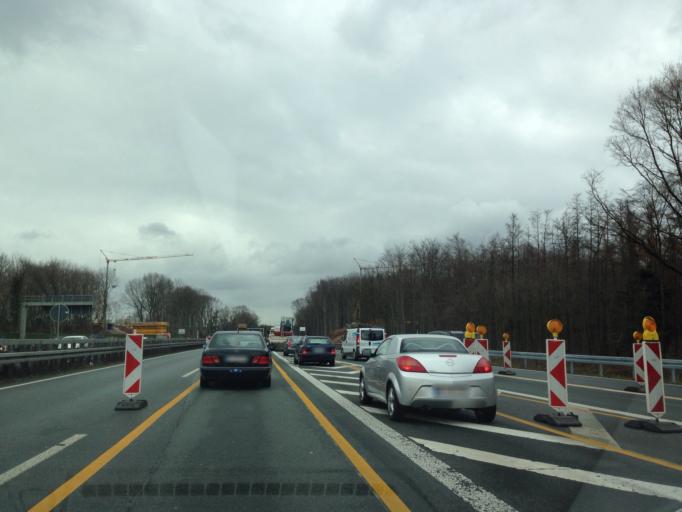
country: DE
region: North Rhine-Westphalia
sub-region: Regierungsbezirk Munster
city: Recklinghausen
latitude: 51.5863
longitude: 7.1884
